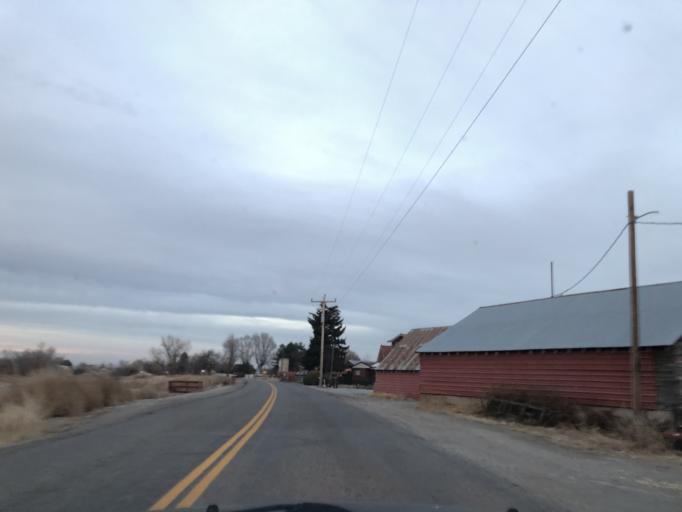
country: US
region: Utah
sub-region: Cache County
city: Benson
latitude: 41.7919
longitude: -111.9069
